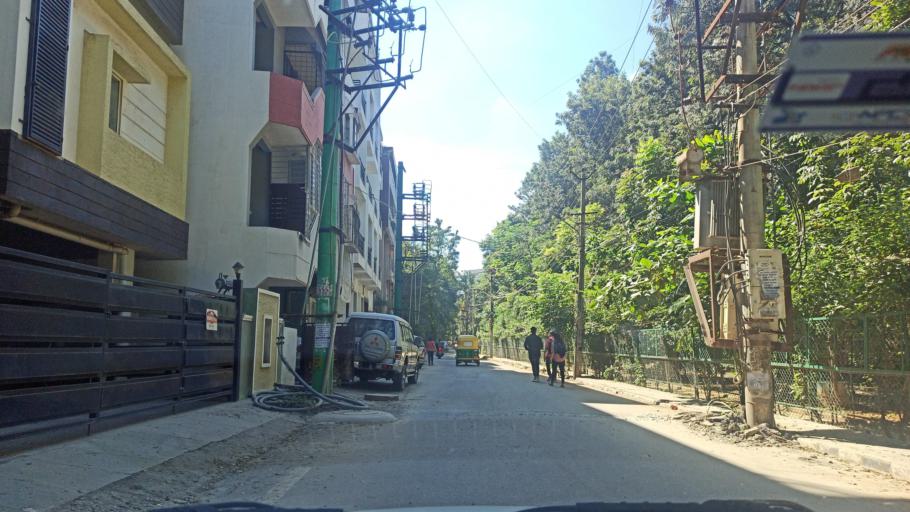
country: IN
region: Karnataka
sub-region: Bangalore Urban
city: Bangalore
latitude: 12.9270
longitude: 77.6719
